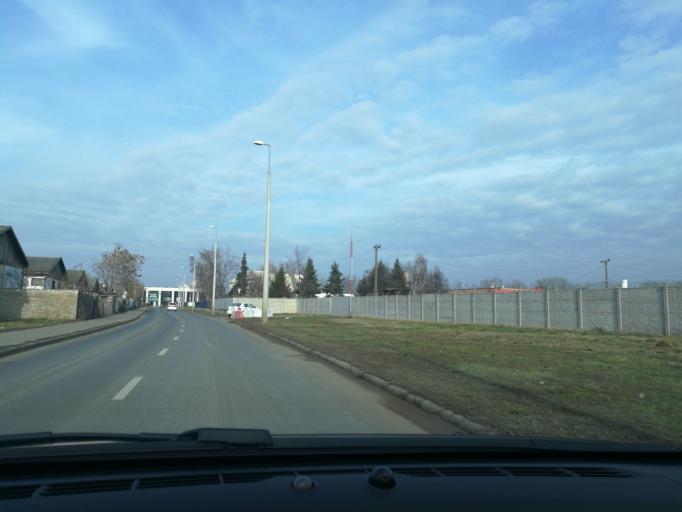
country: HU
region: Szabolcs-Szatmar-Bereg
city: Nyiregyhaza
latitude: 47.9497
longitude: 21.7401
